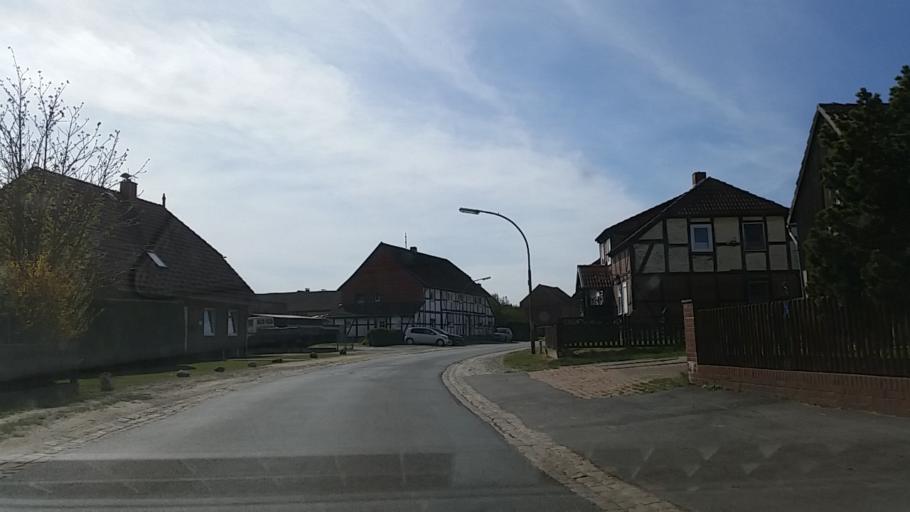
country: DE
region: Lower Saxony
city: Bahrdorf
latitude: 52.3879
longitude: 11.0064
